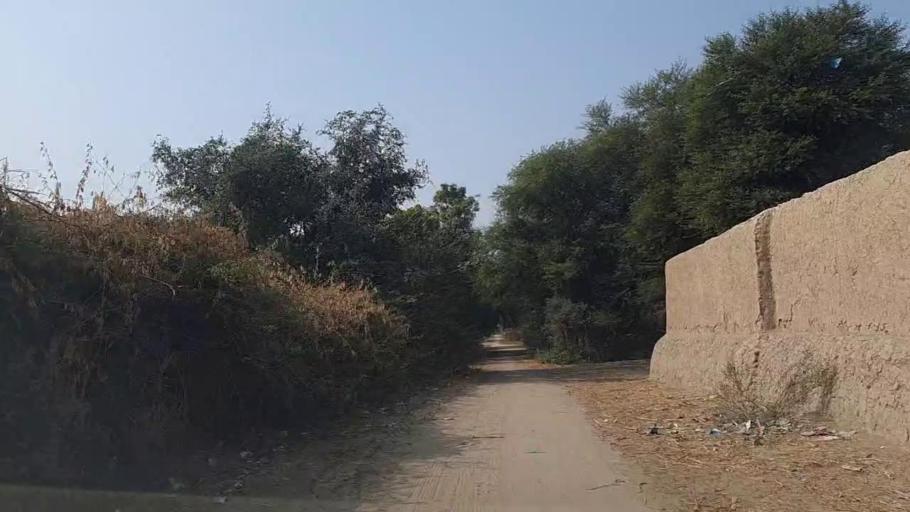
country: PK
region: Sindh
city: Daur
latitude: 26.4268
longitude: 68.4435
